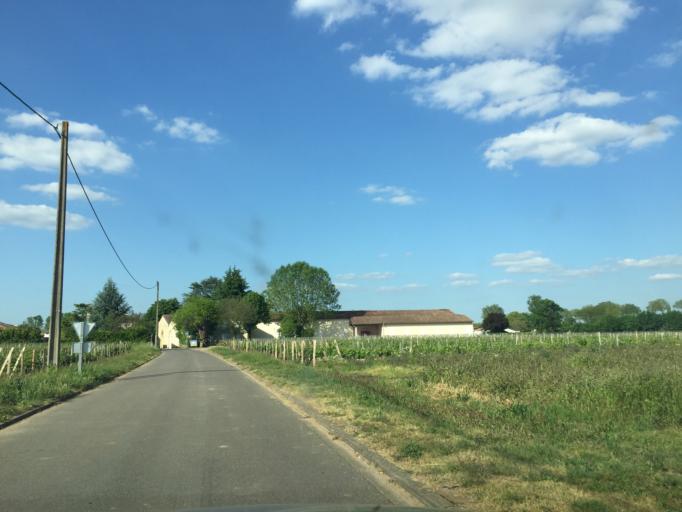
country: FR
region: Aquitaine
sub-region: Departement de la Gironde
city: Libourne
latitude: 44.9332
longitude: -0.2245
